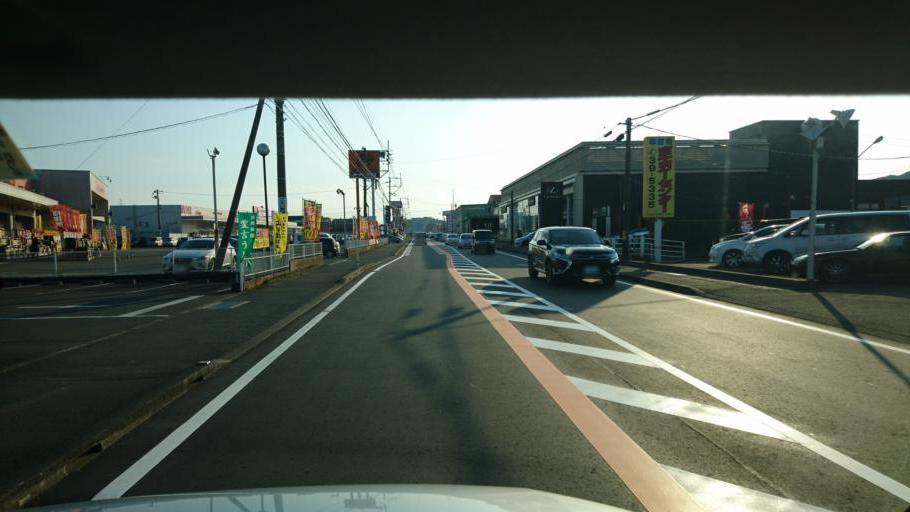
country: JP
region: Miyazaki
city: Miyazaki-shi
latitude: 31.9820
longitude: 131.4472
